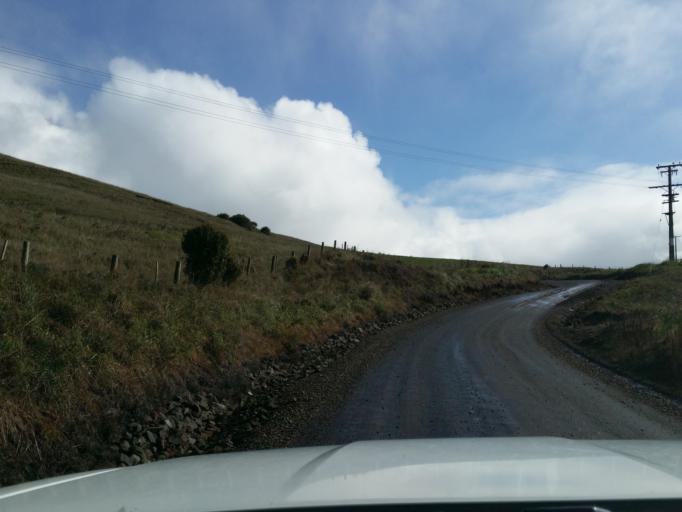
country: NZ
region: Northland
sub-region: Kaipara District
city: Dargaville
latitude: -35.7308
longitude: 173.5748
